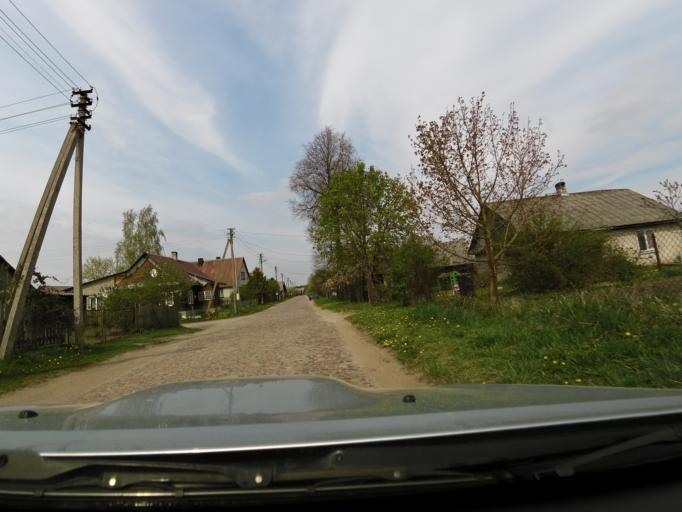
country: LT
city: Baltoji Voke
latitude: 54.4339
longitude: 25.1503
